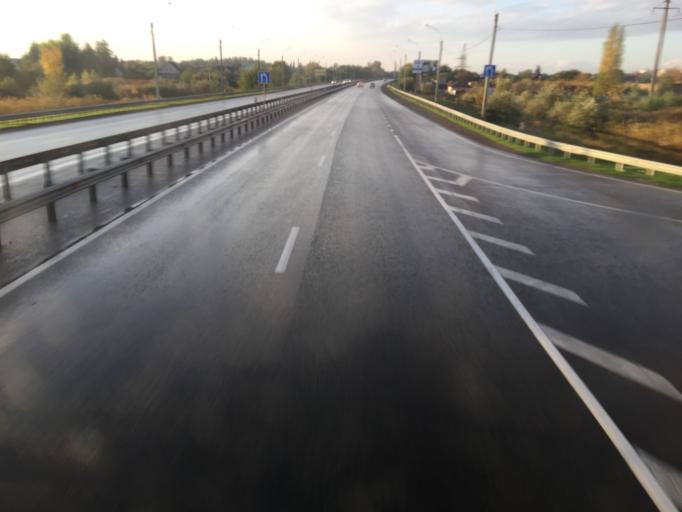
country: RU
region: Rostov
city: Bataysk
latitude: 47.1369
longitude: 39.7762
